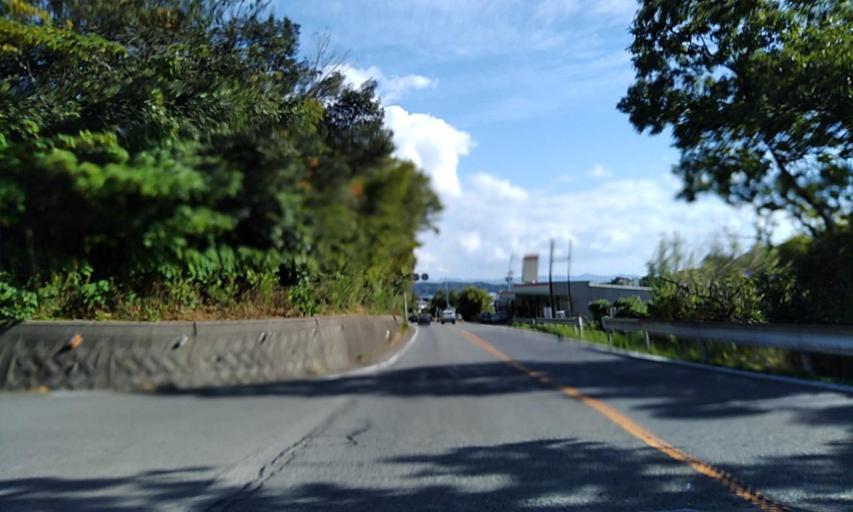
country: JP
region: Wakayama
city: Tanabe
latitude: 33.7796
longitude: 135.3055
